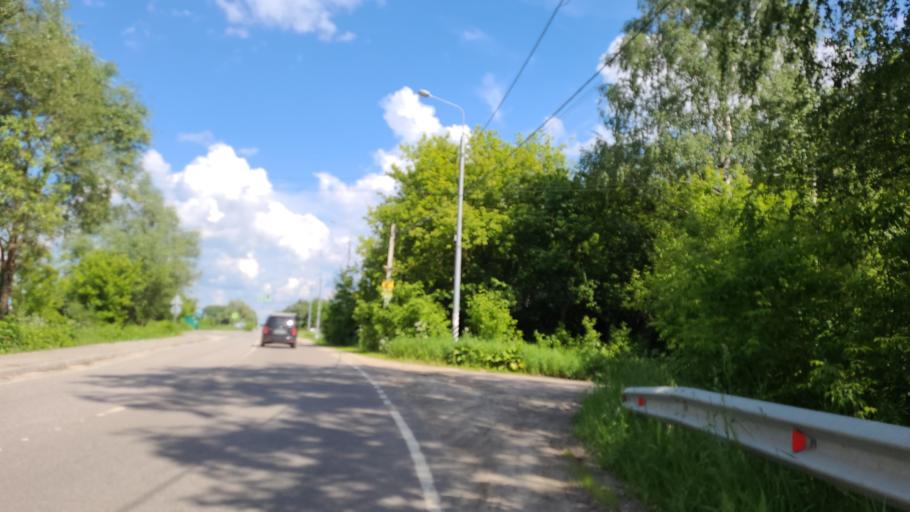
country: RU
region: Moskovskaya
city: Konobeyevo
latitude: 55.4015
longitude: 38.6649
